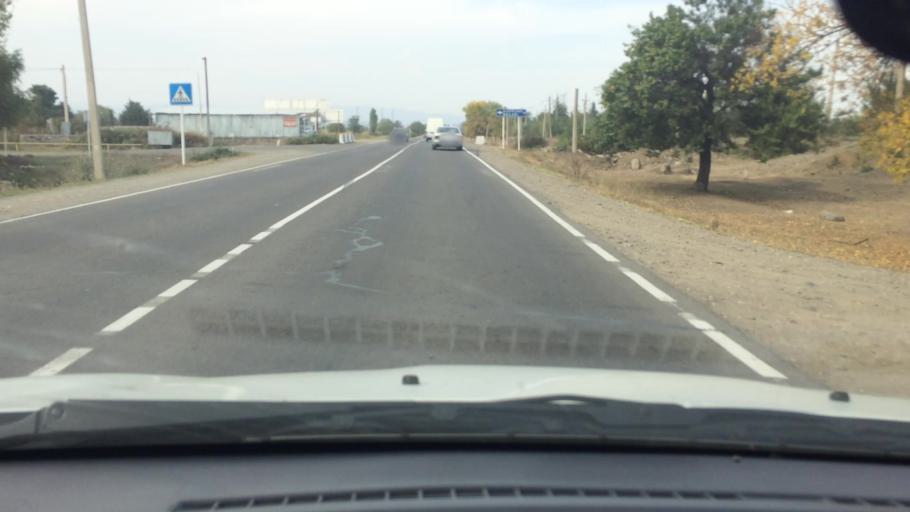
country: GE
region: Kvemo Kartli
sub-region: Marneuli
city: Marneuli
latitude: 41.4216
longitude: 44.8246
